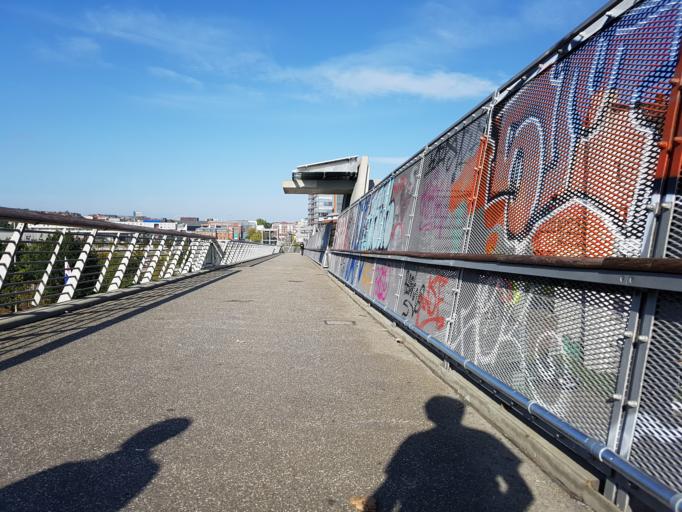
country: DE
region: Schleswig-Holstein
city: Kiel
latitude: 54.3134
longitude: 10.1412
